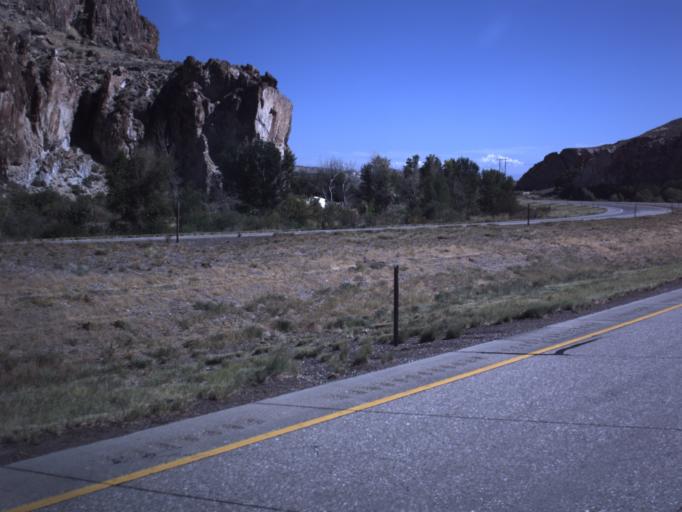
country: US
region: Utah
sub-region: Sevier County
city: Monroe
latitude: 38.5790
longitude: -112.2832
